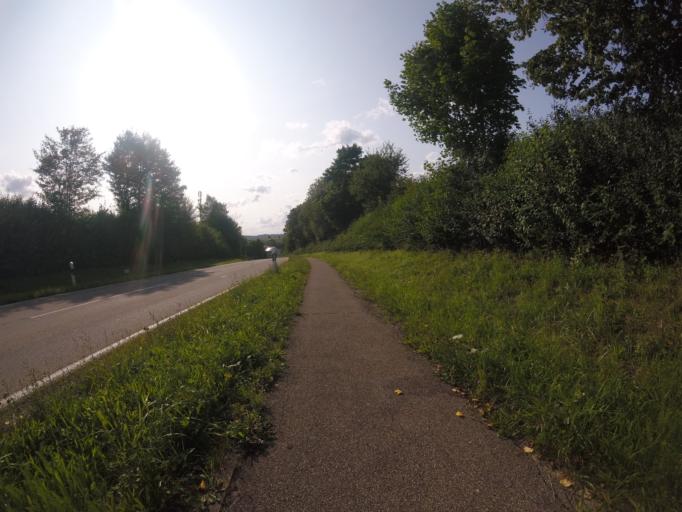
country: DE
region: Baden-Wuerttemberg
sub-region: Regierungsbezirk Stuttgart
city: Aspach
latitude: 48.9912
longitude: 9.3998
